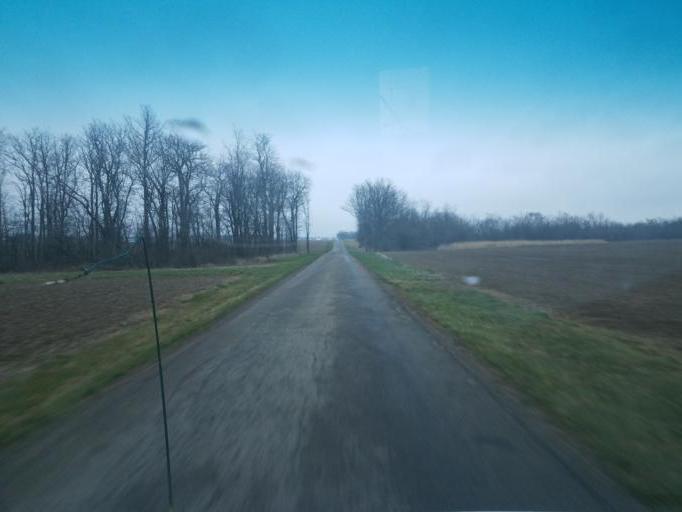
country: US
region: Ohio
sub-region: Defiance County
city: Hicksville
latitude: 41.3391
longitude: -84.7565
